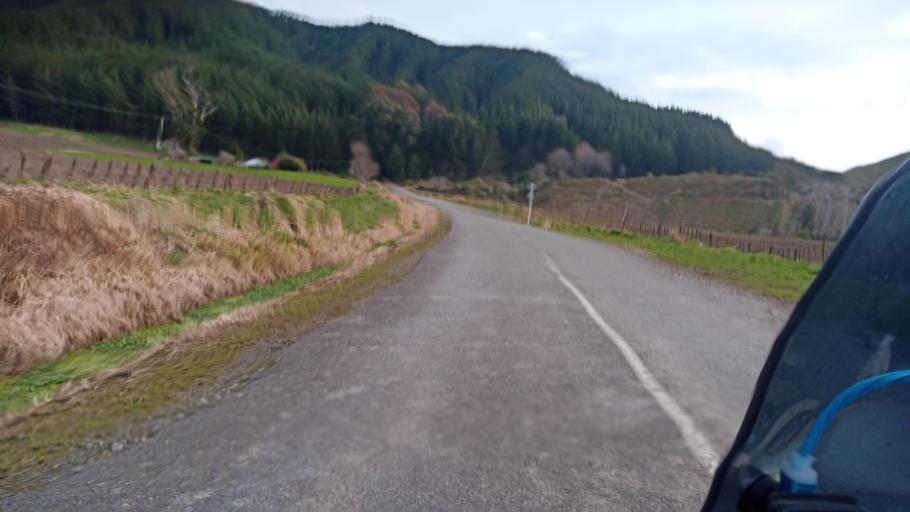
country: NZ
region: Hawke's Bay
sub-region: Wairoa District
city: Wairoa
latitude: -38.8184
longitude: 177.4772
